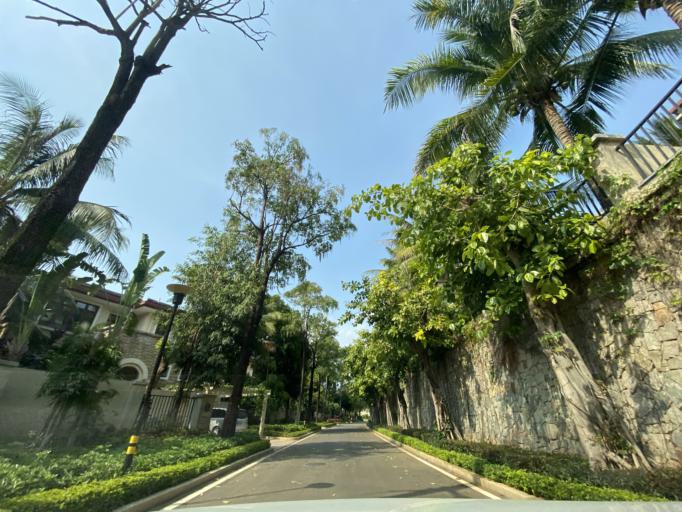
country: CN
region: Hainan
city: Yingzhou
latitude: 18.4100
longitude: 109.8433
